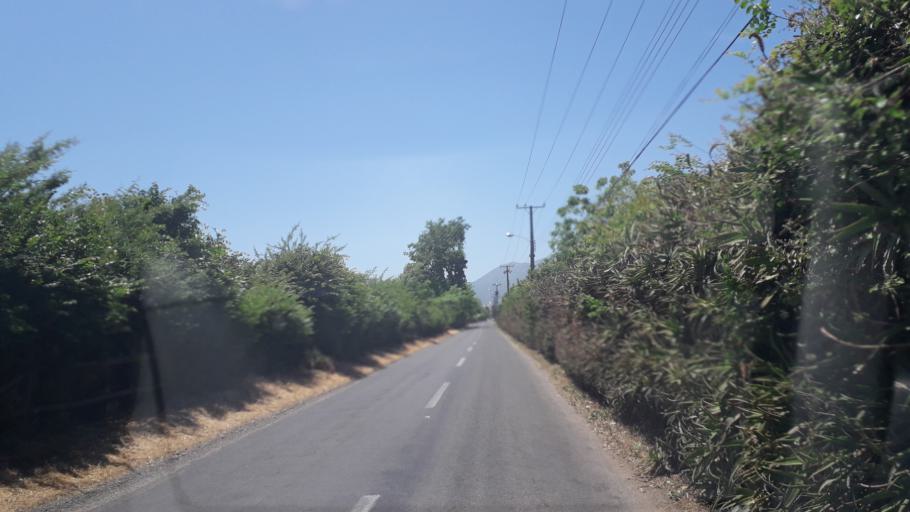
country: CL
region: Valparaiso
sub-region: Provincia de Quillota
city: Quillota
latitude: -32.9240
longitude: -71.2460
